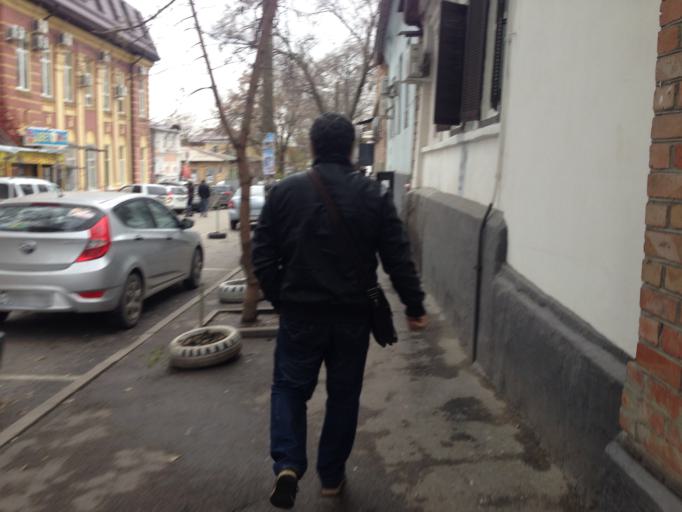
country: RU
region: Rostov
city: Rostov-na-Donu
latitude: 47.2167
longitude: 39.7161
